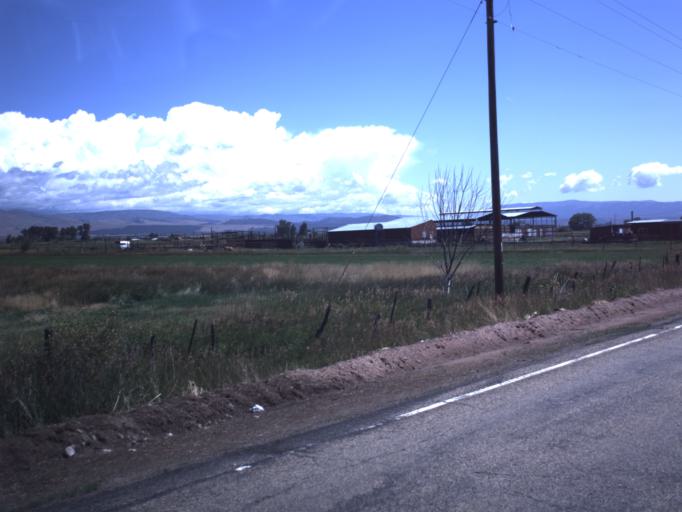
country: US
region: Utah
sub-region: Duchesne County
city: Roosevelt
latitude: 40.4329
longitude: -109.9839
